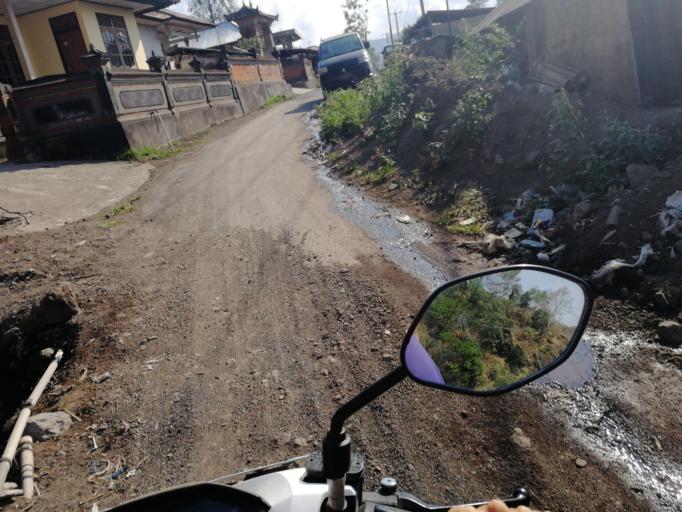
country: ID
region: Bali
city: Banjar Trunyan
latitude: -8.2632
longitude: 115.4221
